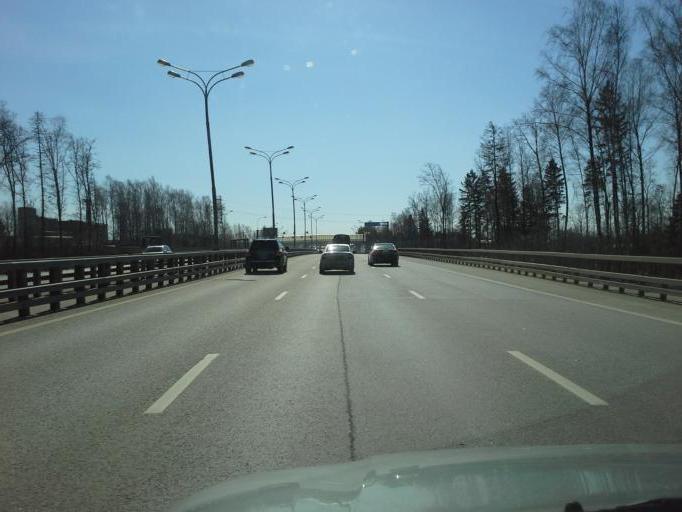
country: RU
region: Moskovskaya
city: Annino
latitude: 55.6038
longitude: 37.2469
